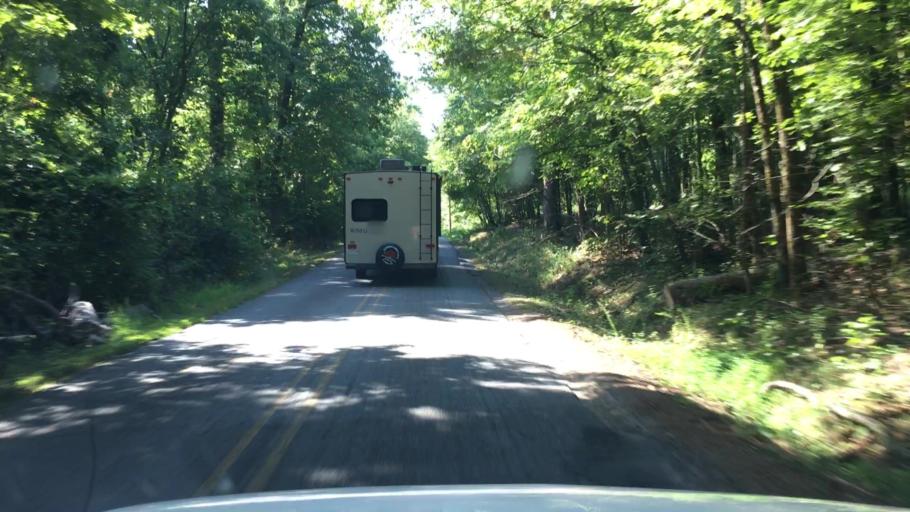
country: US
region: Arkansas
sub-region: Garland County
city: Piney
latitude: 34.5384
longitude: -93.3419
